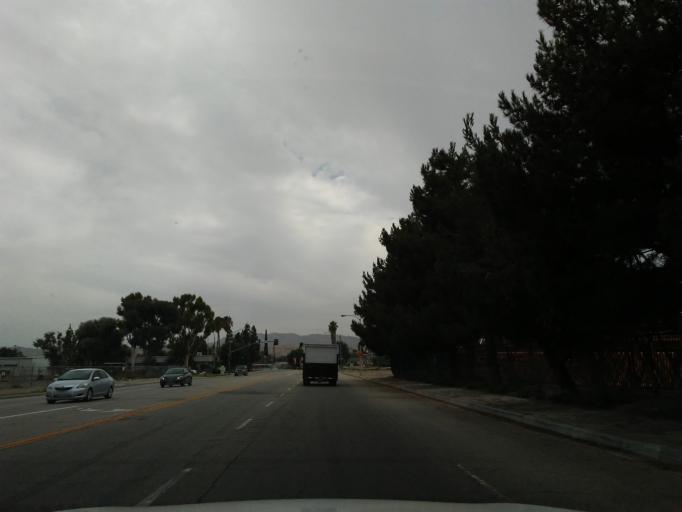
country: US
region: California
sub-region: San Bernardino County
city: Loma Linda
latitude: 34.0757
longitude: -117.2598
